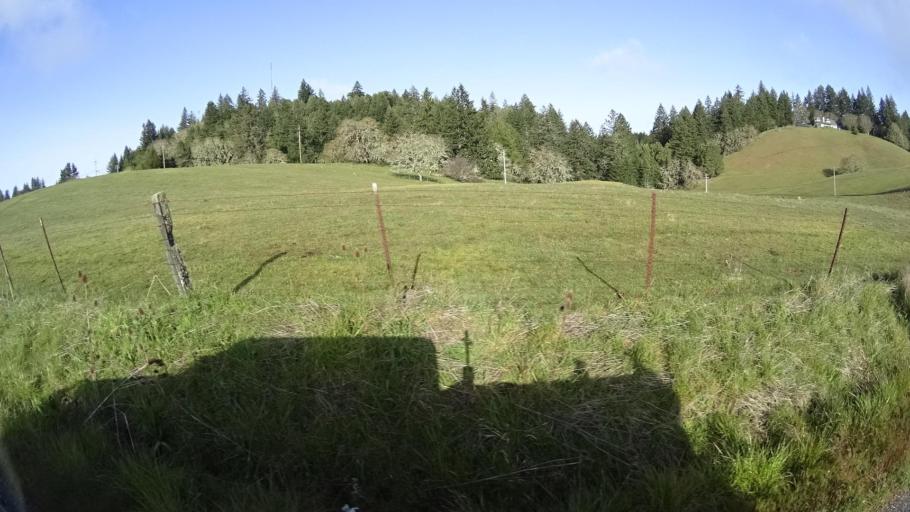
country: US
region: California
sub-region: Humboldt County
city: Blue Lake
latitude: 40.7321
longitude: -123.9476
